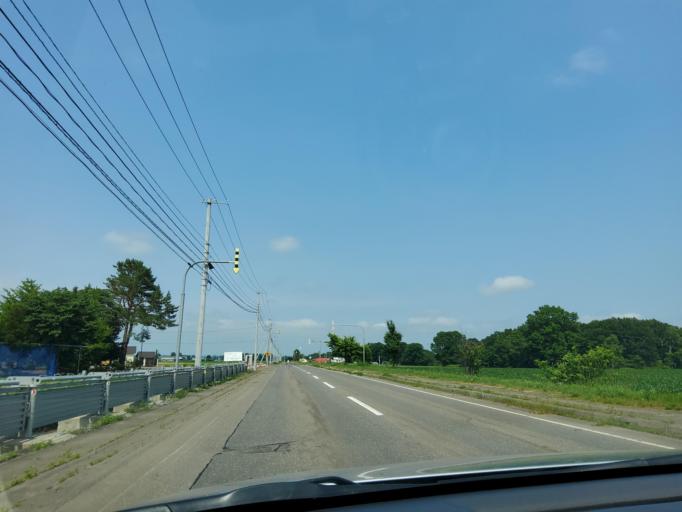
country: JP
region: Hokkaido
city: Obihiro
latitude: 42.8681
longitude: 143.0190
